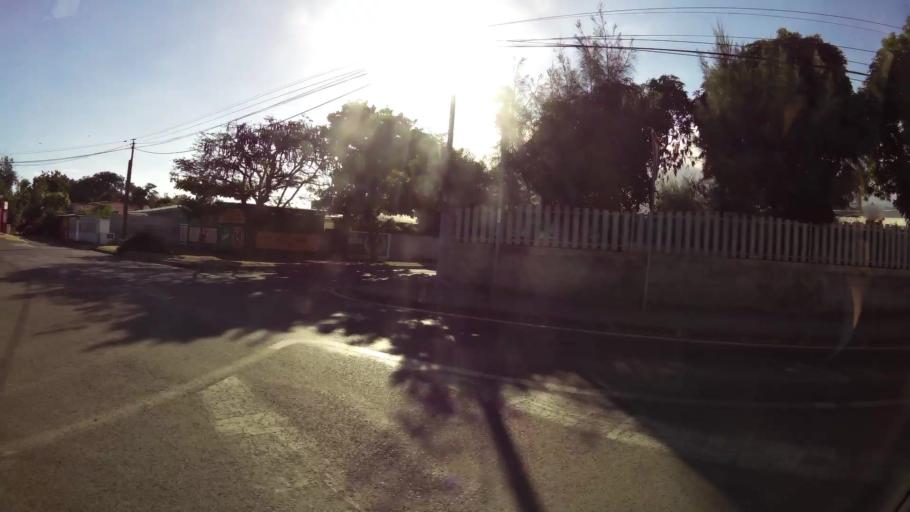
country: RE
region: Reunion
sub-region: Reunion
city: Saint-Louis
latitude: -21.2936
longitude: 55.3988
